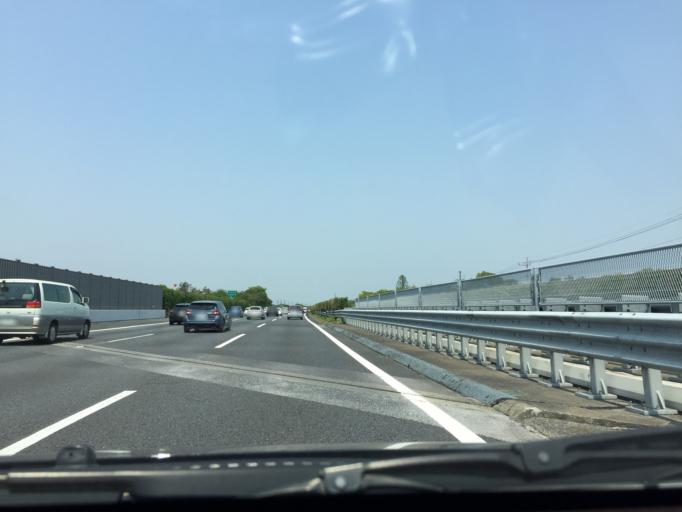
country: JP
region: Saitama
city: Kazo
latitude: 36.1530
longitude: 139.5967
